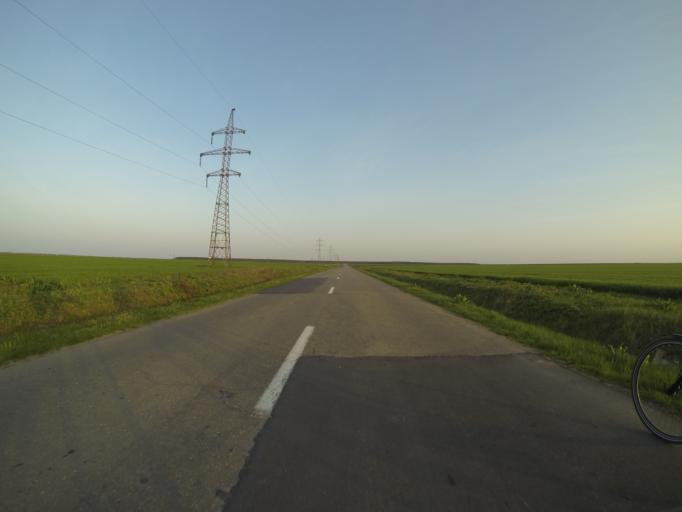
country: RO
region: Dolj
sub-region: Comuna Segarcea
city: Segarcea
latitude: 44.0783
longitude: 23.7893
